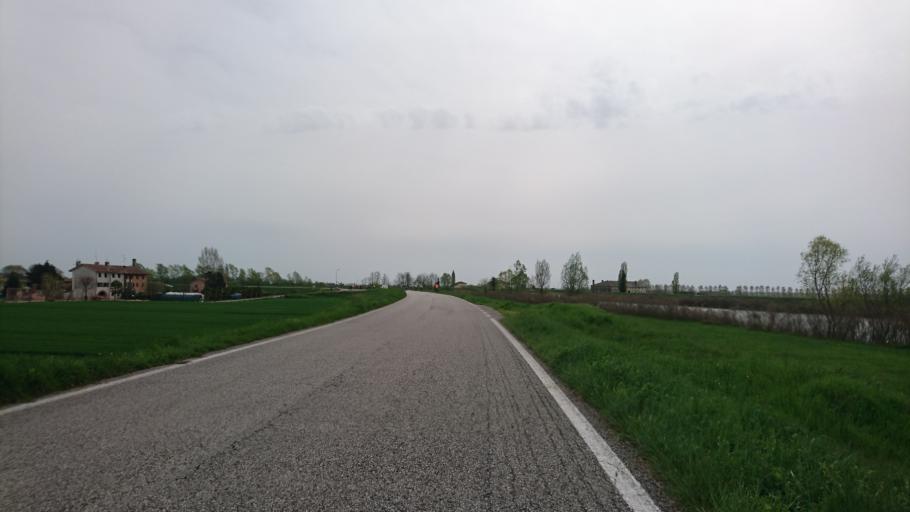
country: IT
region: Veneto
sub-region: Provincia di Venezia
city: La Salute di Livenza
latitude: 45.6471
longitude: 12.8182
